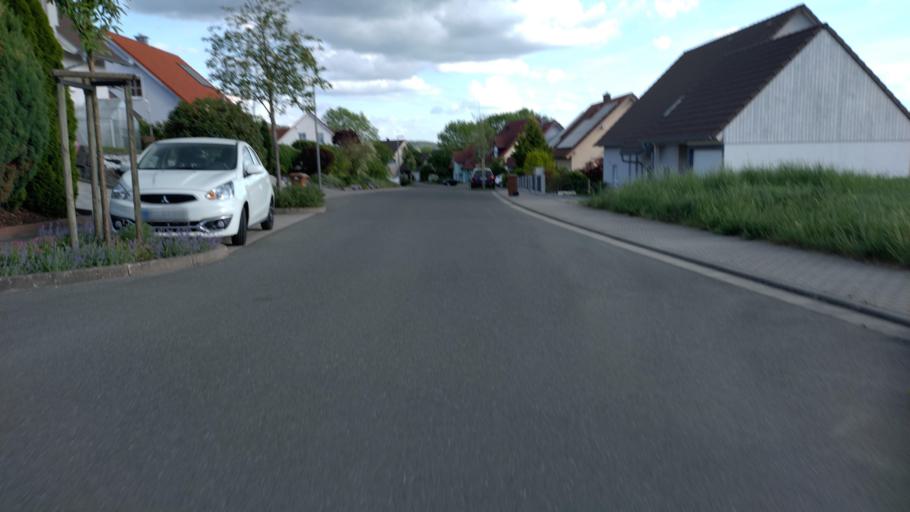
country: DE
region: Bavaria
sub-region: Upper Franconia
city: Bindlach
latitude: 49.9861
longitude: 11.6186
